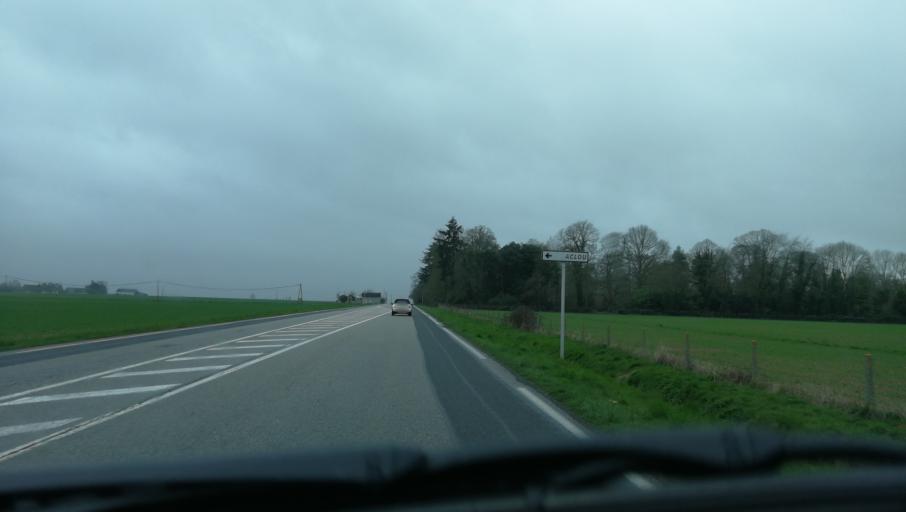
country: FR
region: Haute-Normandie
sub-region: Departement de l'Eure
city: Brionne
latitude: 49.1805
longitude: 0.7045
